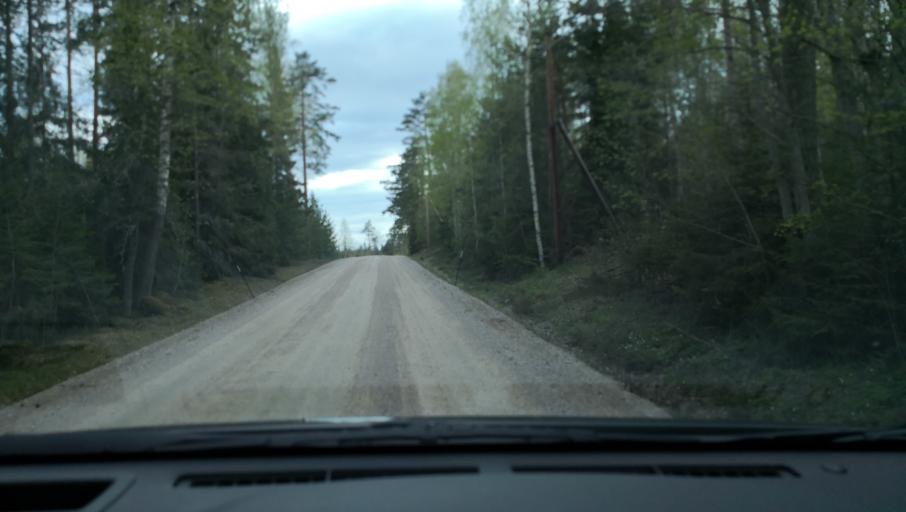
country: SE
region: Vaestmanland
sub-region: Norbergs Kommun
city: Norberg
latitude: 60.0911
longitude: 15.8519
